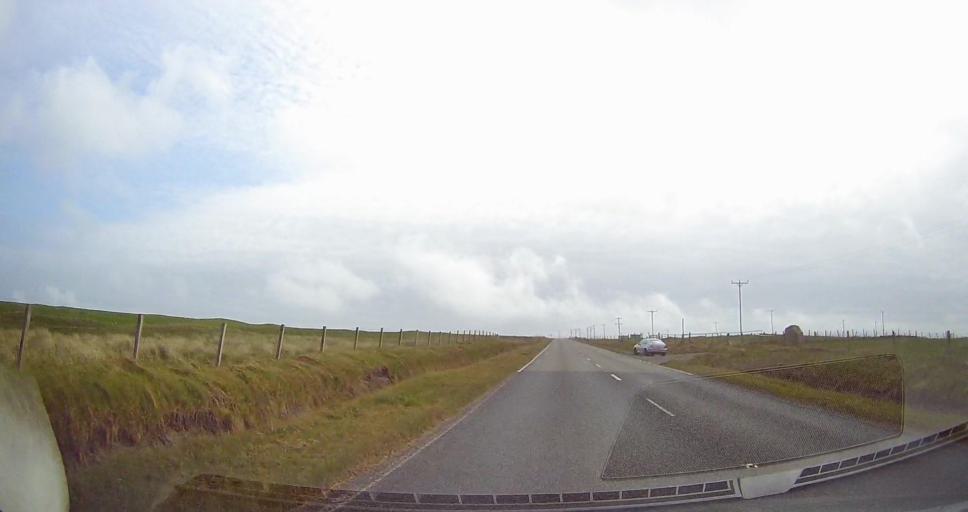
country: GB
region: Scotland
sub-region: Shetland Islands
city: Sandwick
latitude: 59.9026
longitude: -1.3025
